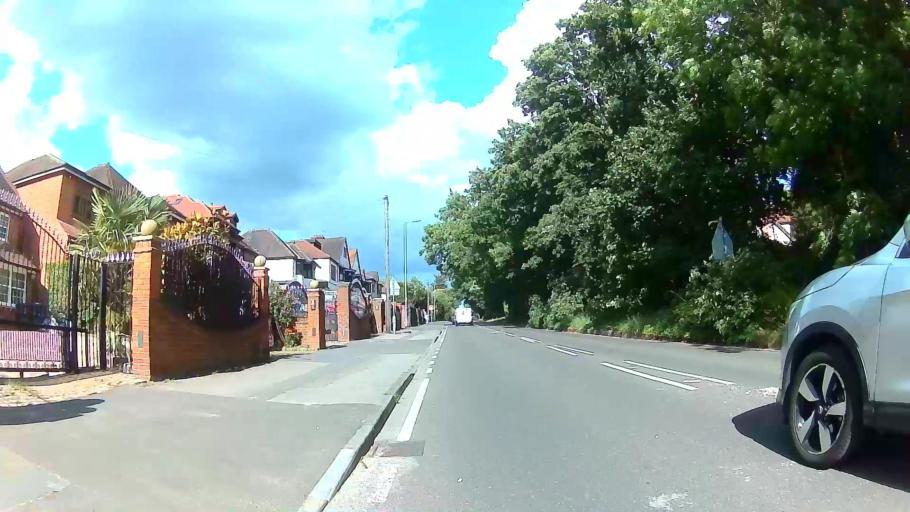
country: GB
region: England
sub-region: Essex
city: Chigwell
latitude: 51.6079
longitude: 0.0665
